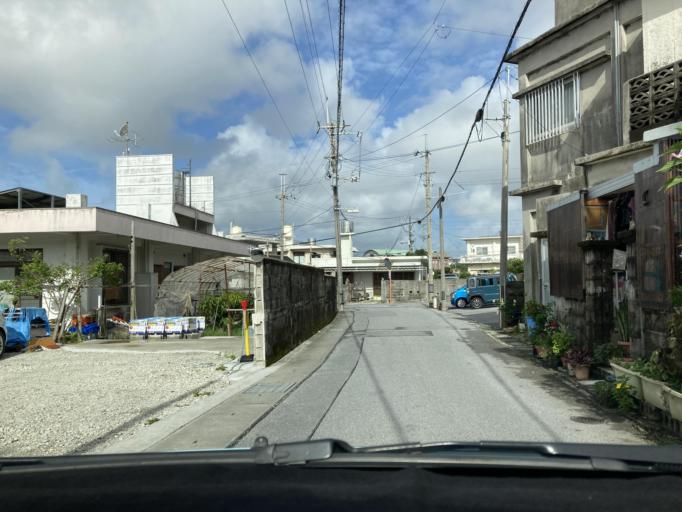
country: JP
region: Okinawa
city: Naha-shi
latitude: 26.2038
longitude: 127.7283
